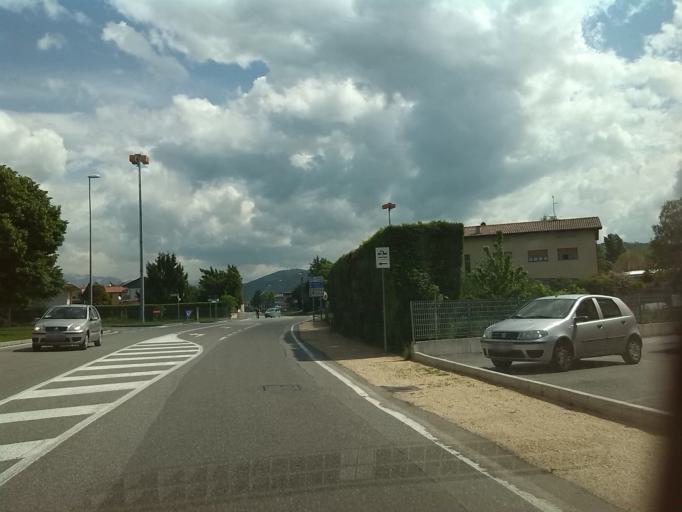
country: IT
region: Friuli Venezia Giulia
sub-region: Provincia di Udine
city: Cividale del Friuli
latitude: 46.0854
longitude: 13.4299
